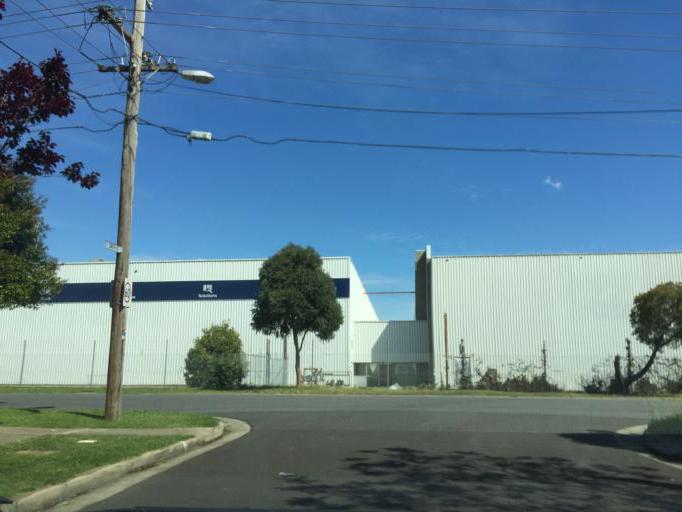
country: AU
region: Victoria
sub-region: Maribyrnong
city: Maribyrnong
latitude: -37.7795
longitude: 144.8801
